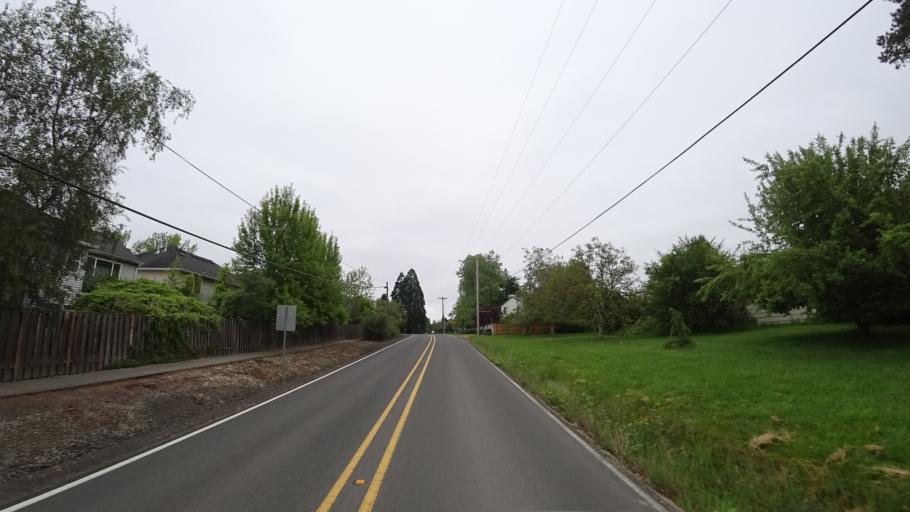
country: US
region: Oregon
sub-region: Washington County
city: Bethany
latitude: 45.5504
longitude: -122.8574
